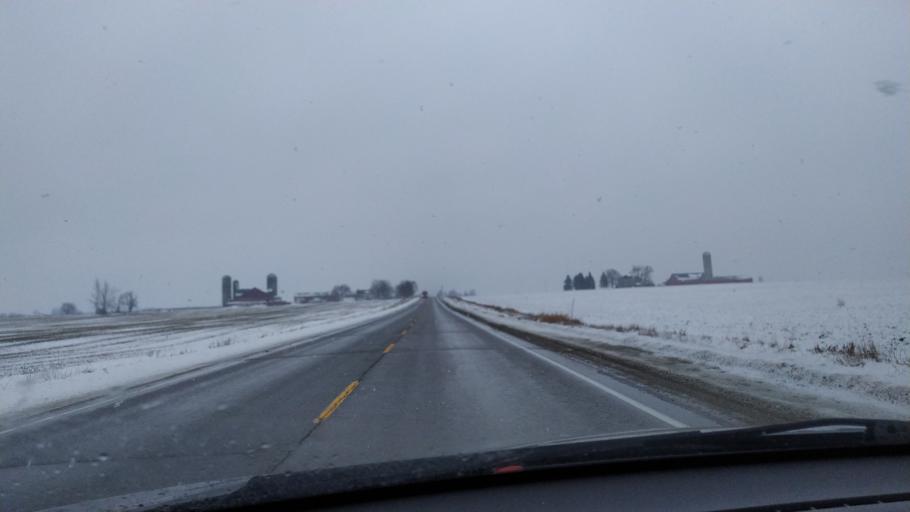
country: CA
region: Ontario
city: Stratford
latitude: 43.5222
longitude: -80.8776
